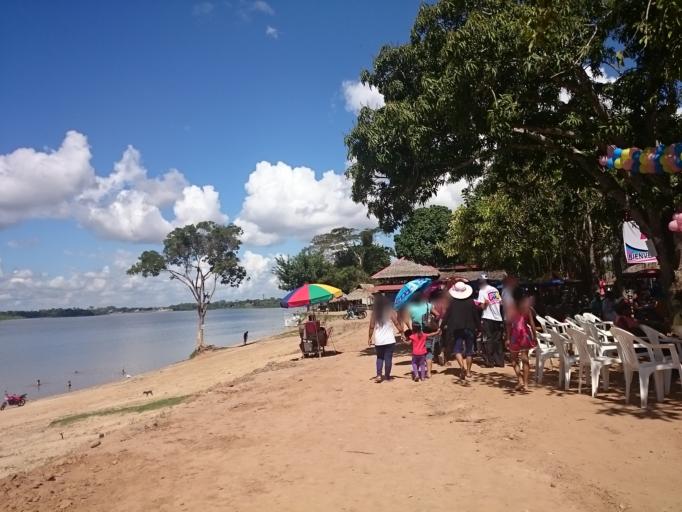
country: PE
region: Ucayali
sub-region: Provincia de Coronel Portillo
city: Puerto Callao
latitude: -8.3381
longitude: -74.5946
